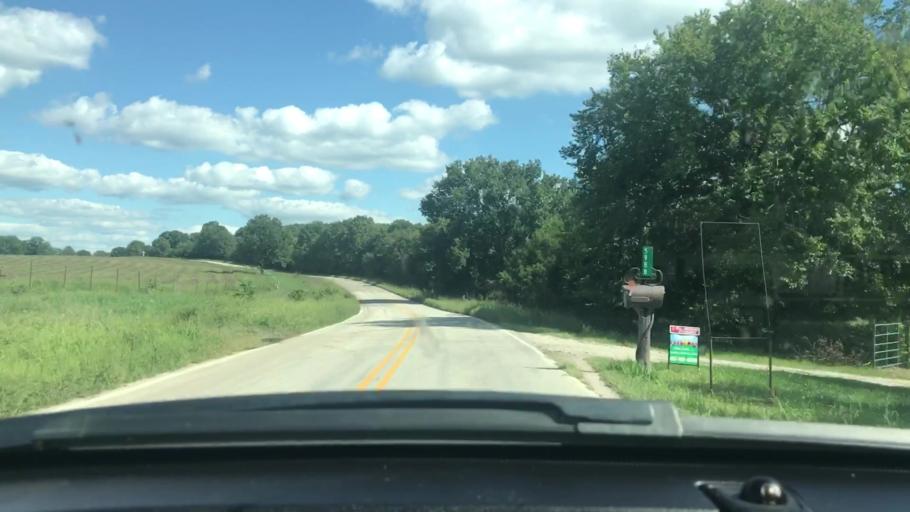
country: US
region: Missouri
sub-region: Wright County
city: Hartville
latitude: 37.3783
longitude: -92.4342
